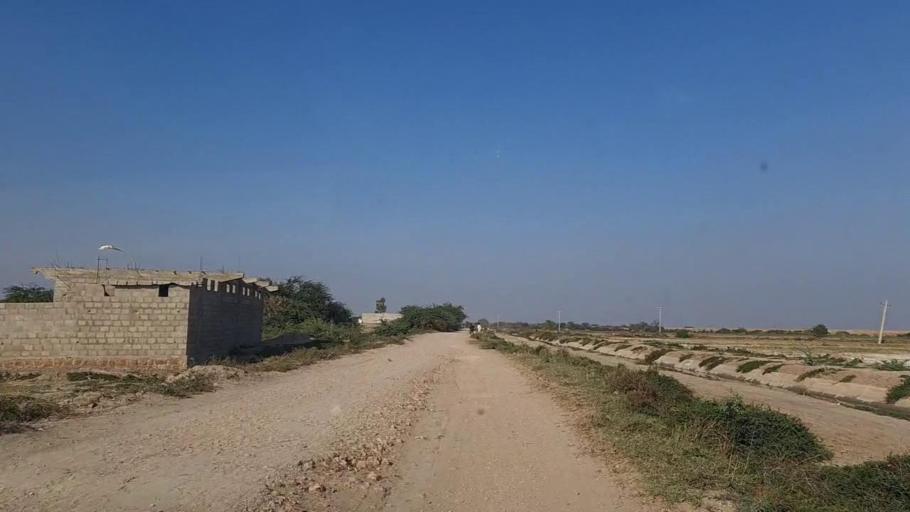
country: PK
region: Sindh
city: Thatta
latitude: 24.7397
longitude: 67.9672
